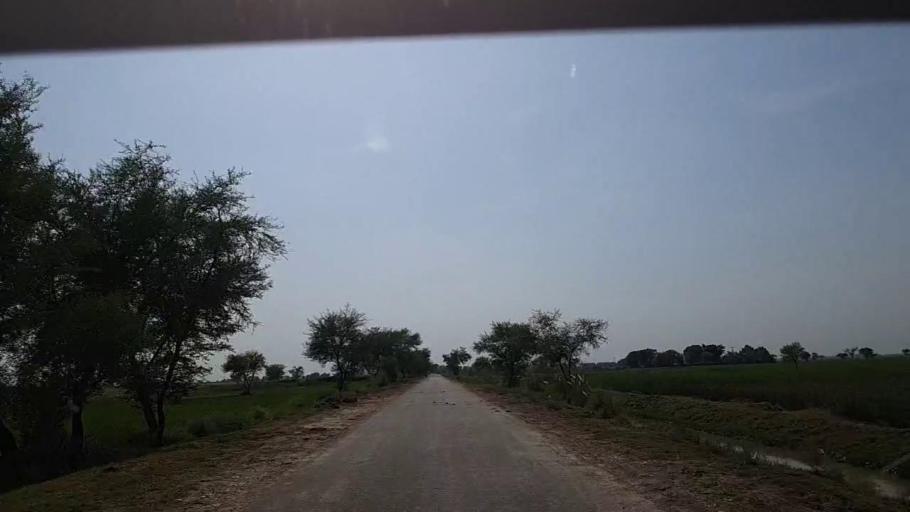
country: PK
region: Sindh
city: Khanpur
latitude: 27.8430
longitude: 69.3854
